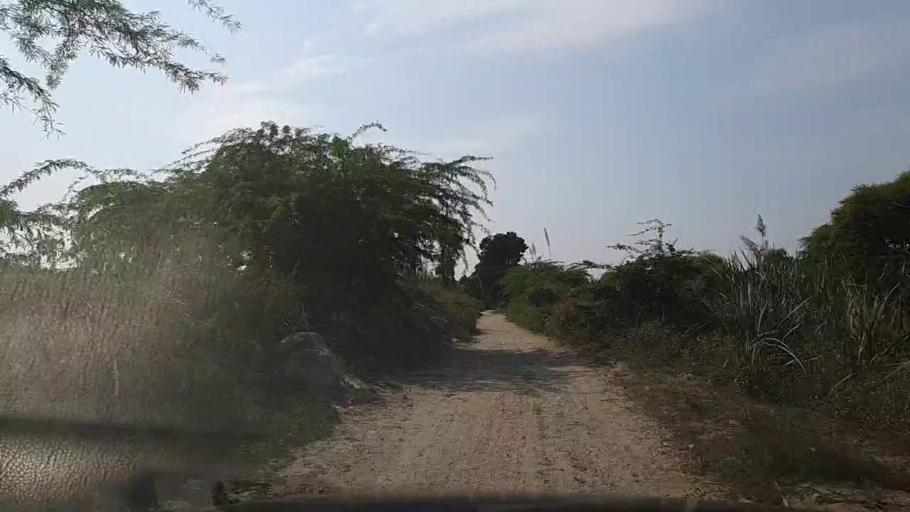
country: PK
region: Sindh
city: Thatta
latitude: 24.7635
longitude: 67.7861
